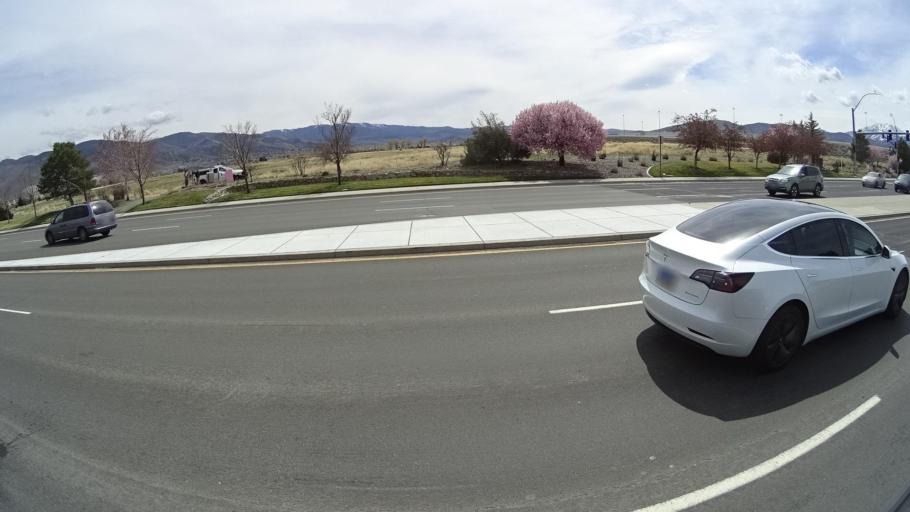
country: US
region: Nevada
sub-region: Washoe County
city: Sparks
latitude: 39.4246
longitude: -119.7477
